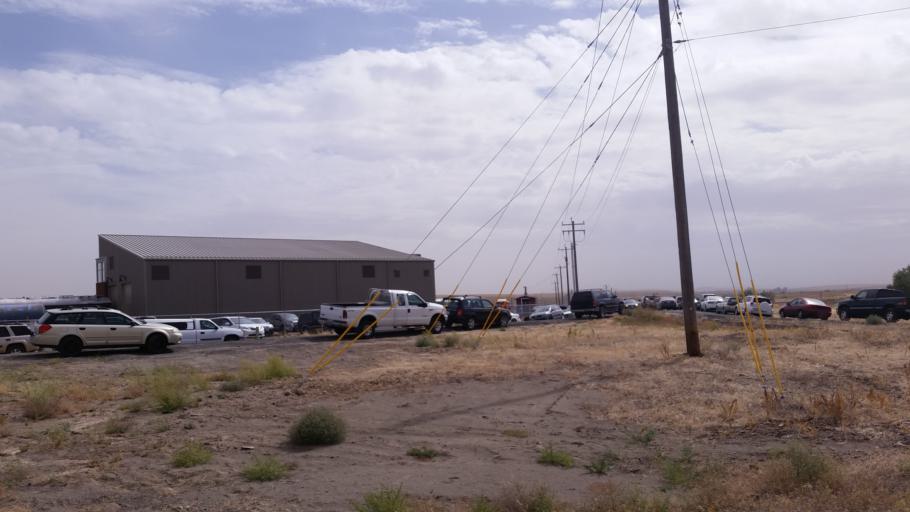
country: US
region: Washington
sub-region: Lincoln County
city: Davenport
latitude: 47.6646
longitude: -117.9380
